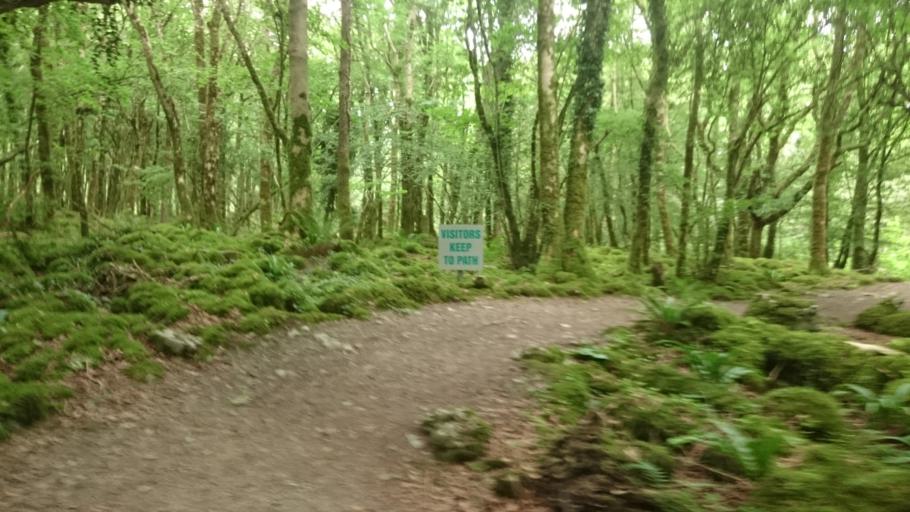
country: IE
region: Munster
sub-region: An Clar
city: Sixmilebridge
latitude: 52.8110
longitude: -8.7966
